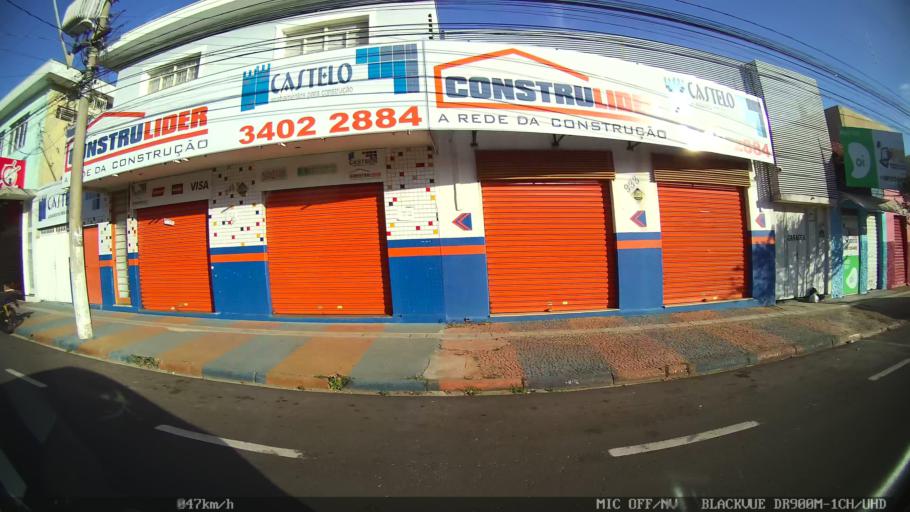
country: BR
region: Sao Paulo
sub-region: Franca
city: Franca
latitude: -20.5268
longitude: -47.3832
